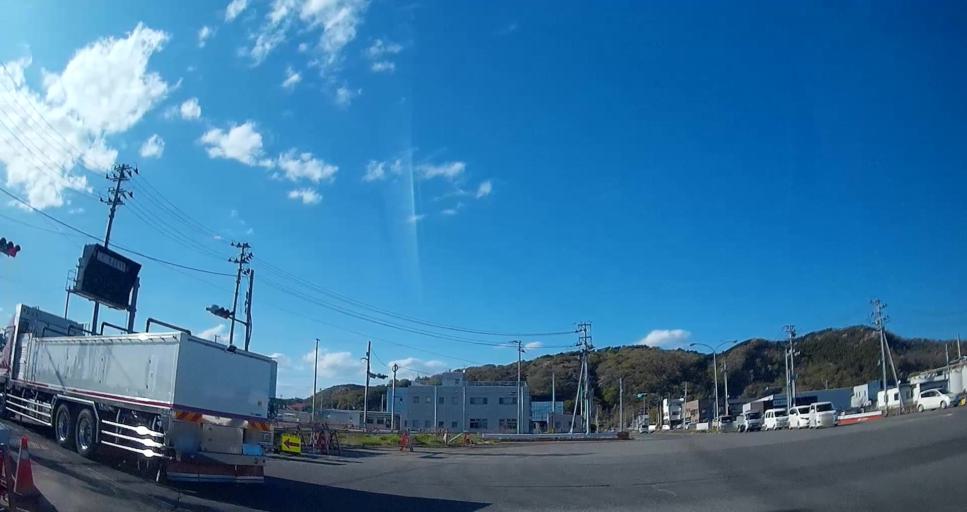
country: JP
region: Miyagi
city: Ishinomaki
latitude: 38.4154
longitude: 141.3263
